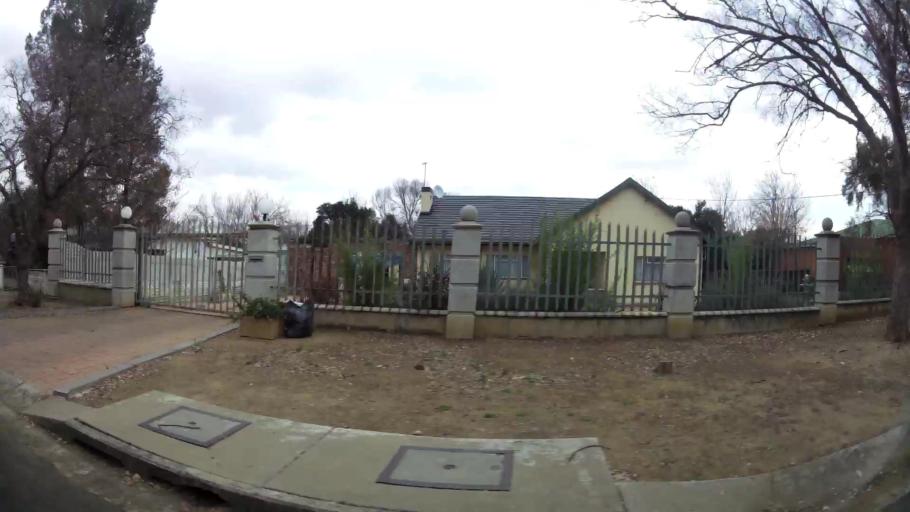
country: ZA
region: Orange Free State
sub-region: Fezile Dabi District Municipality
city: Kroonstad
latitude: -27.6850
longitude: 27.2318
